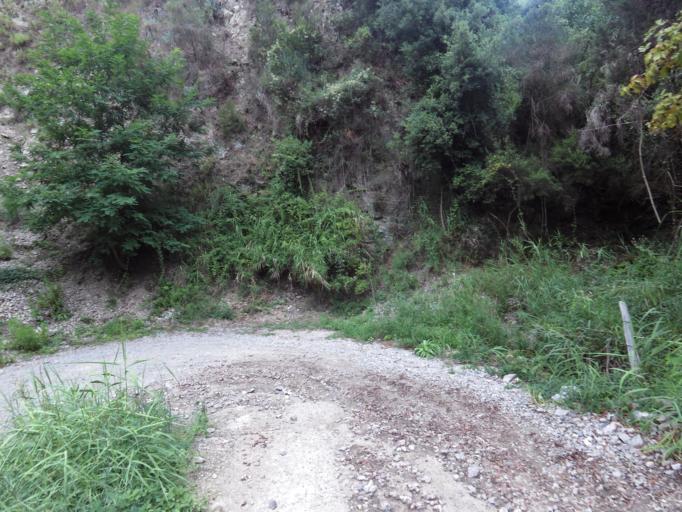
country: IT
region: Calabria
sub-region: Provincia di Reggio Calabria
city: Bivongi
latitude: 38.4906
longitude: 16.4296
